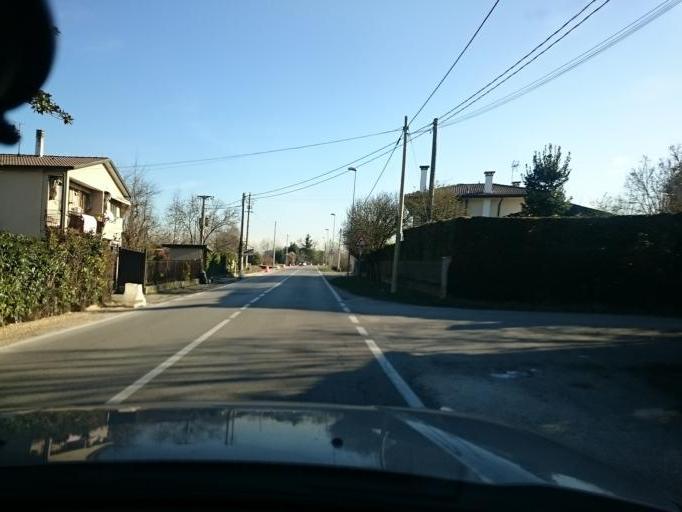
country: IT
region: Veneto
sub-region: Provincia di Padova
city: Albignasego
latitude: 45.3506
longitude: 11.8875
